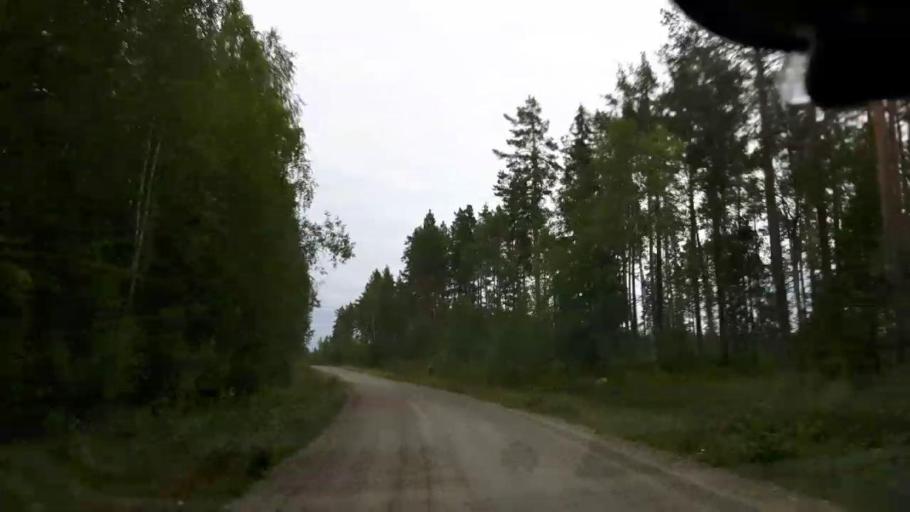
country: SE
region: Vaesternorrland
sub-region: Ange Kommun
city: Ange
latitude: 62.8155
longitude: 15.7131
